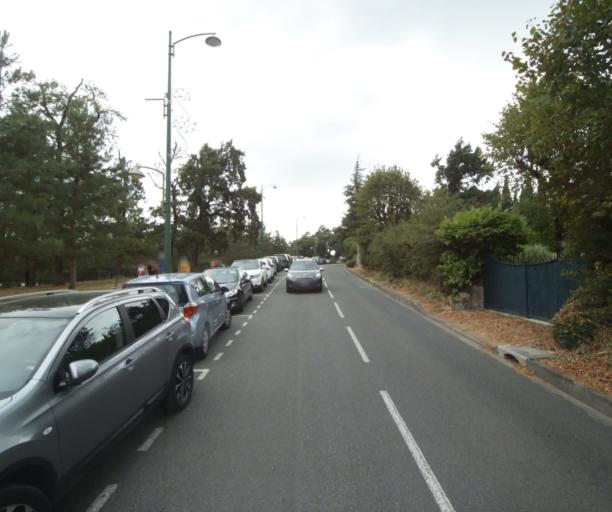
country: FR
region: Midi-Pyrenees
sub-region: Departement de la Haute-Garonne
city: Revel
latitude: 43.4402
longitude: 2.0228
